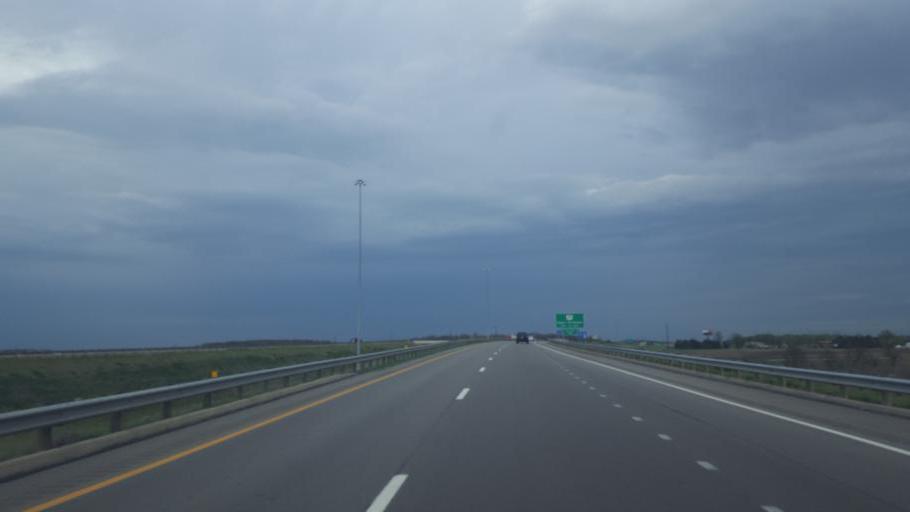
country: US
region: Ohio
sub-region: Wyandot County
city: Upper Sandusky
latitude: 40.8575
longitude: -83.3125
